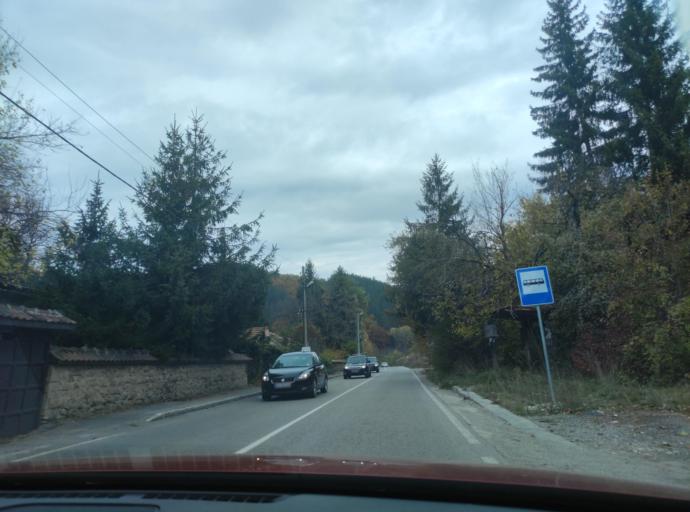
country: BG
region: Sofiya
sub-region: Obshtina Godech
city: Godech
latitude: 42.9734
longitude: 23.1400
